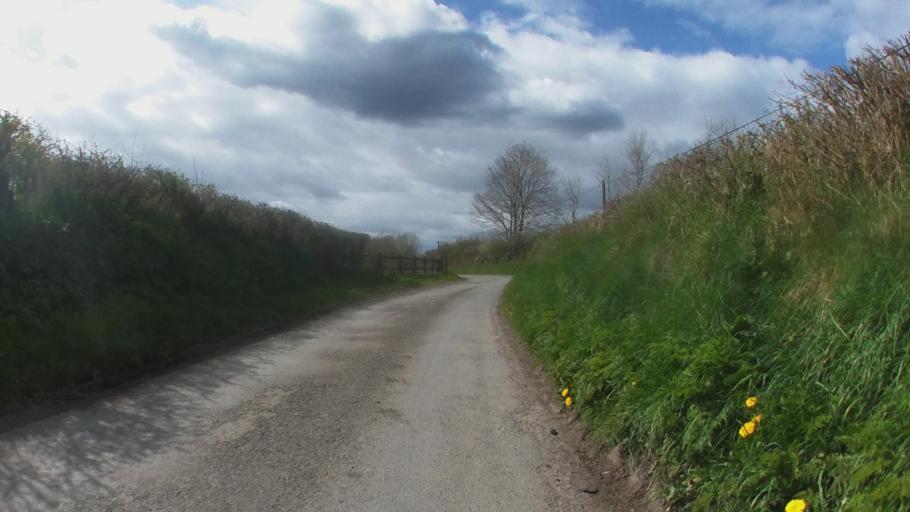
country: IE
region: Leinster
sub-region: Kilkenny
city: Kilkenny
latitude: 52.7215
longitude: -7.2260
